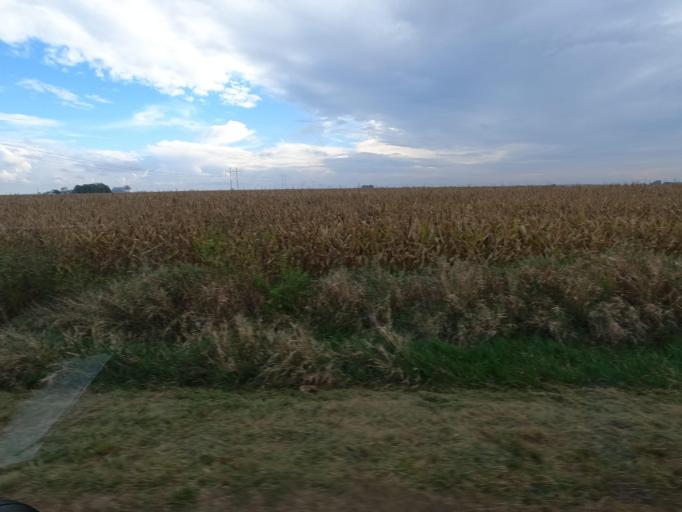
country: US
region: Iowa
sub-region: Henry County
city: Mount Pleasant
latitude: 40.7846
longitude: -91.6451
